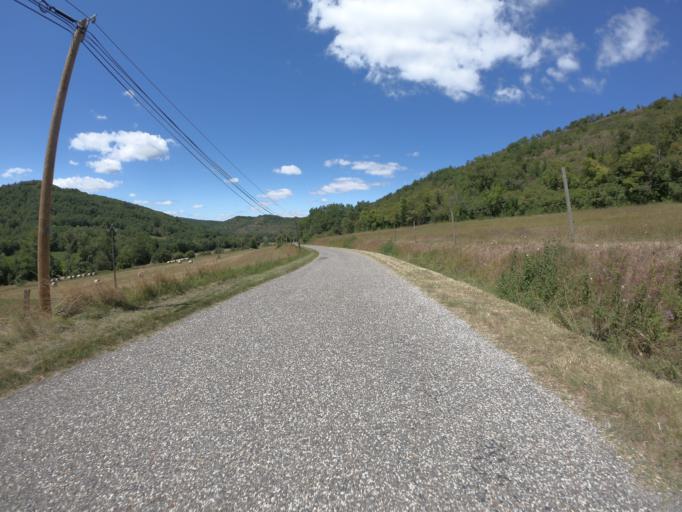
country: FR
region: Midi-Pyrenees
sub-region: Departement de l'Ariege
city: Mirepoix
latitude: 43.0486
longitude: 1.8213
